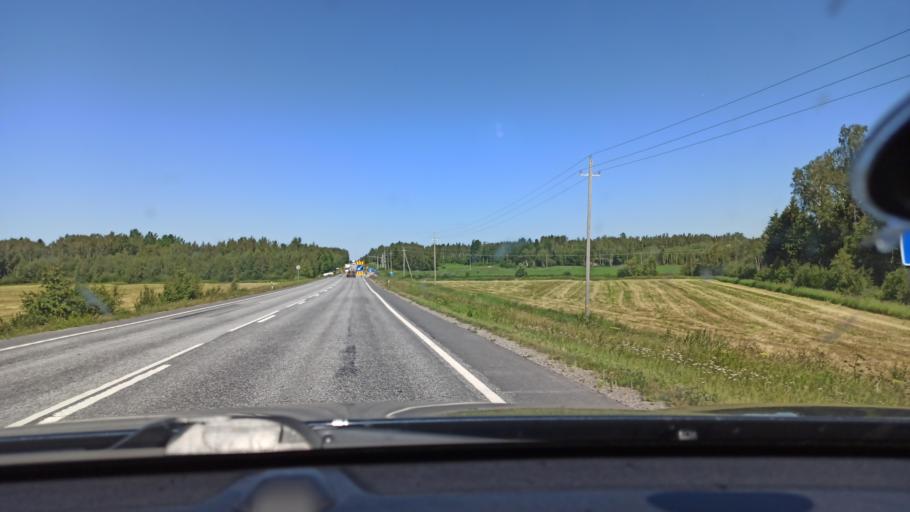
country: FI
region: Ostrobothnia
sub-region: Vaasa
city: Voera
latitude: 63.2365
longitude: 22.2543
